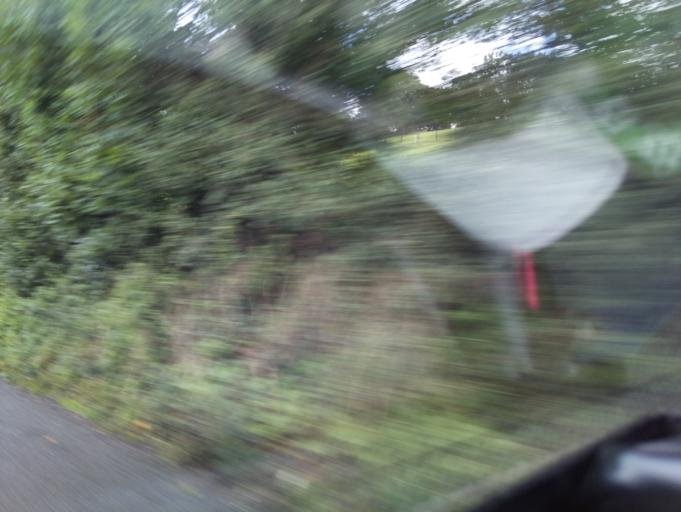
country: GB
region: England
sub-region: Devon
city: Modbury
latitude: 50.3306
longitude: -3.8456
